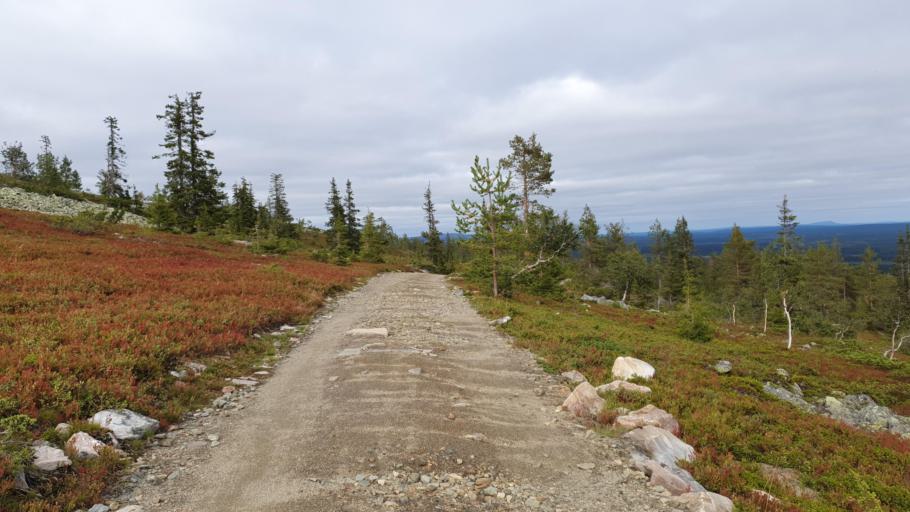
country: FI
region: Lapland
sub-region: Tunturi-Lappi
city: Kolari
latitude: 67.5638
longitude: 24.2557
